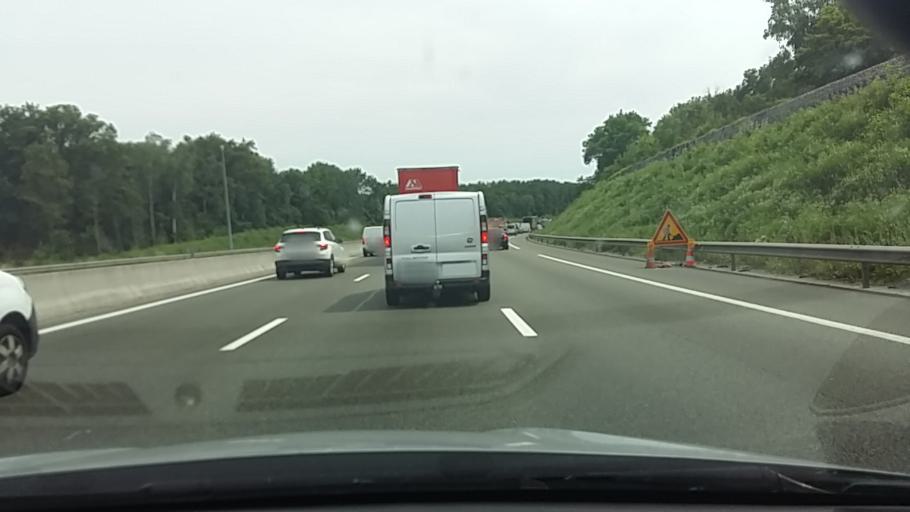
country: FR
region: Ile-de-France
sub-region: Departement de Seine-et-Marne
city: Emerainville
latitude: 48.8123
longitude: 2.6288
